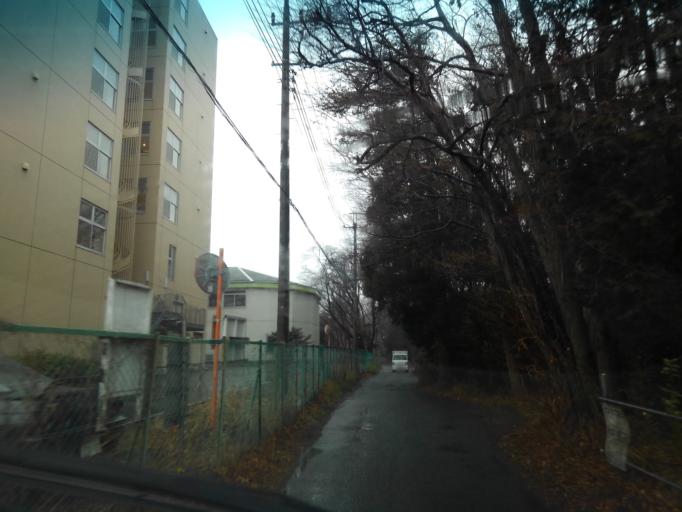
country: JP
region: Saitama
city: Tokorozawa
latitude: 35.8029
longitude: 139.4264
